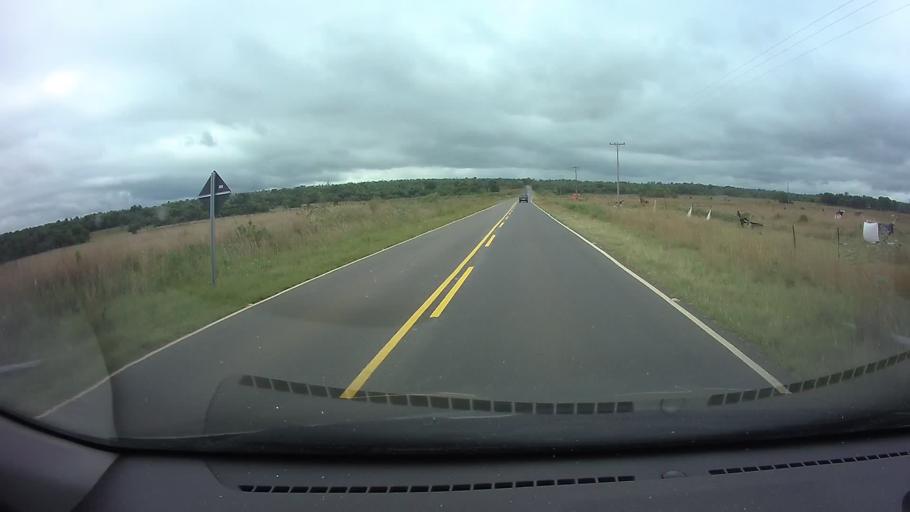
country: PY
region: Paraguari
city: Yaguaron
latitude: -25.7130
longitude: -57.3398
